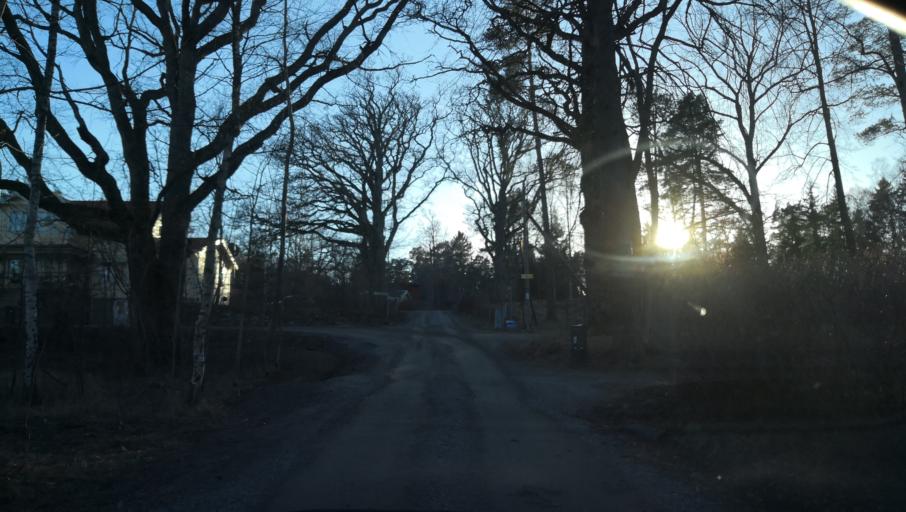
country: SE
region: Stockholm
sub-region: Varmdo Kommun
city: Mortnas
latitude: 59.3303
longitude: 18.4341
